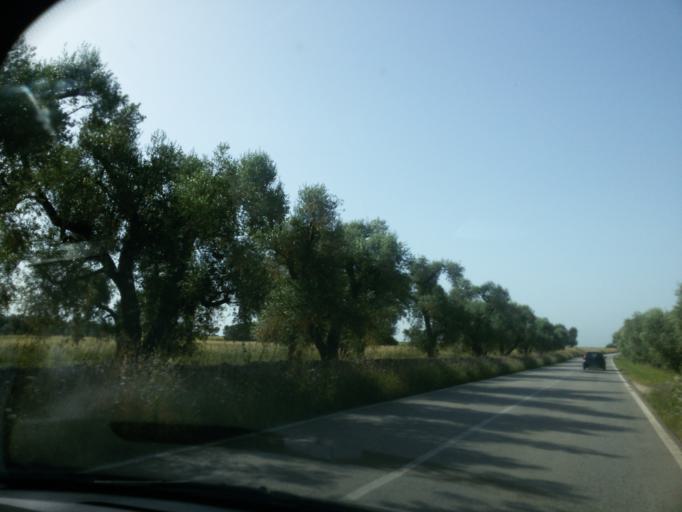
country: IT
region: Apulia
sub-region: Provincia di Brindisi
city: Mesagne
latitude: 40.5123
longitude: 17.8268
